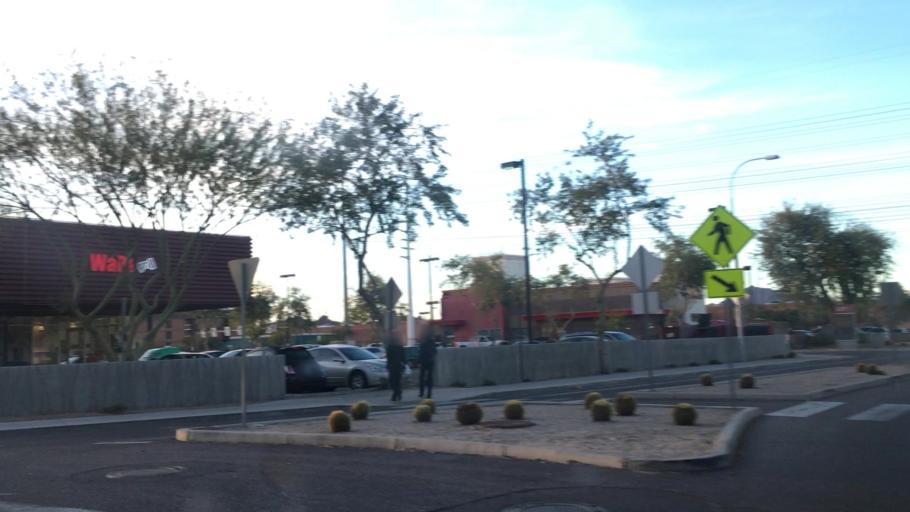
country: US
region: Arizona
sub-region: Maricopa County
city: Tempe
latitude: 33.4342
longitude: -111.9249
